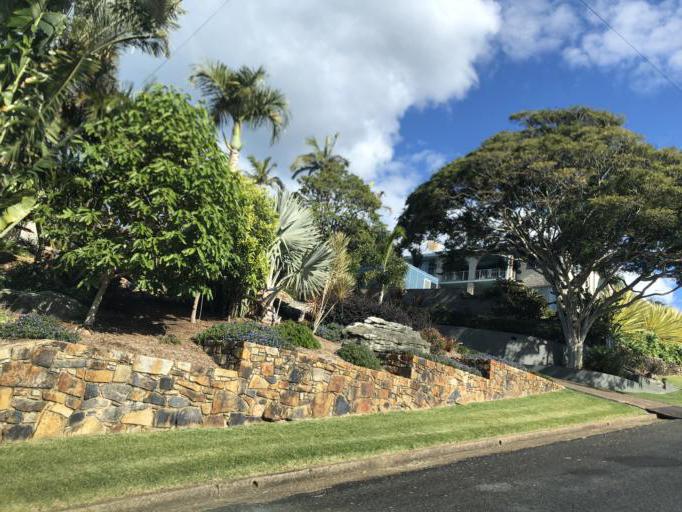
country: AU
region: New South Wales
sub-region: Coffs Harbour
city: Coffs Harbour
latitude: -30.2758
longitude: 153.1352
